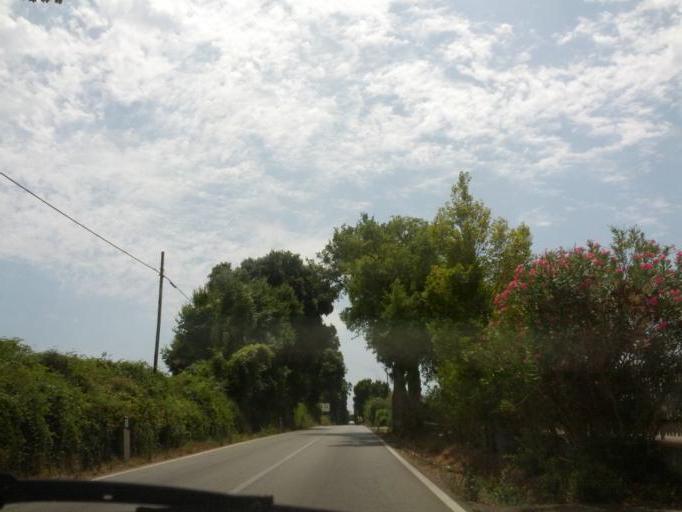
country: IT
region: Latium
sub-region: Provincia di Latina
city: Sperlonga
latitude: 41.3022
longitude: 13.3980
